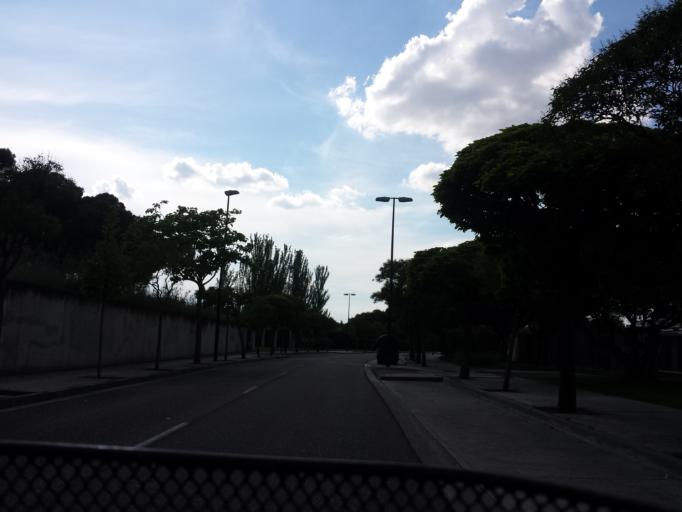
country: ES
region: Aragon
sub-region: Provincia de Zaragoza
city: Montecanal
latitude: 41.6305
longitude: -0.9187
